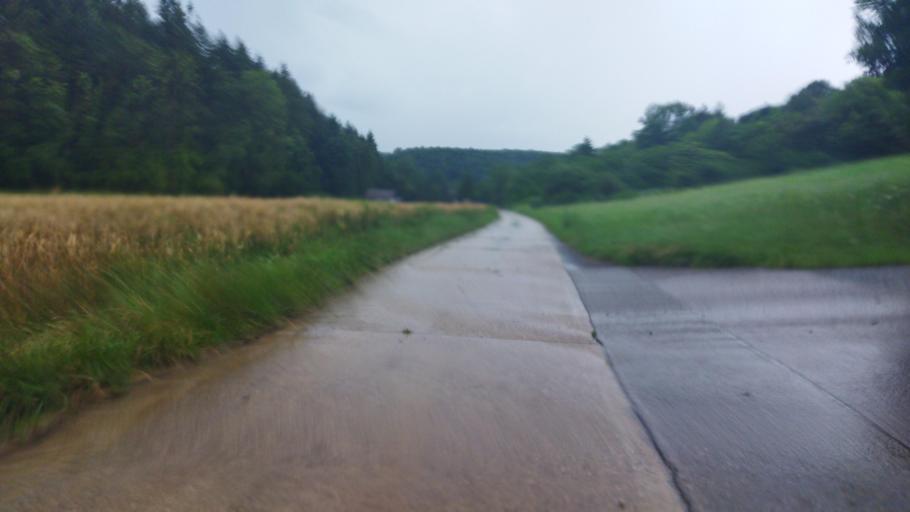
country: DE
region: Baden-Wuerttemberg
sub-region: Regierungsbezirk Stuttgart
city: Ittlingen
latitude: 49.2057
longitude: 8.9415
